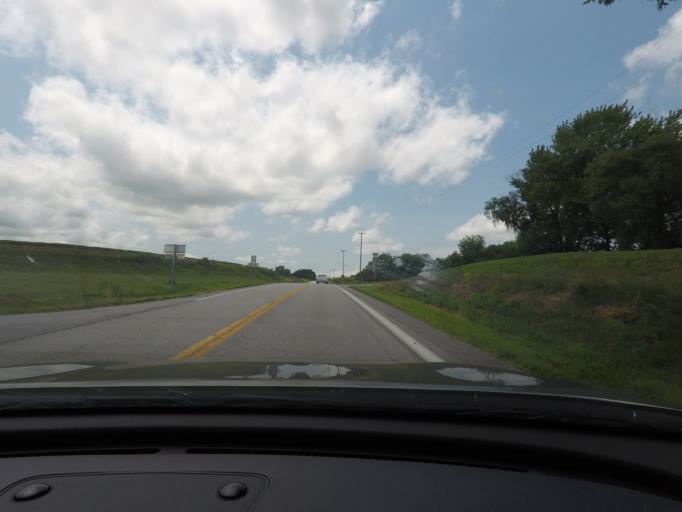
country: US
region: Missouri
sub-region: Carroll County
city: Carrollton
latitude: 39.2040
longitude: -93.4450
